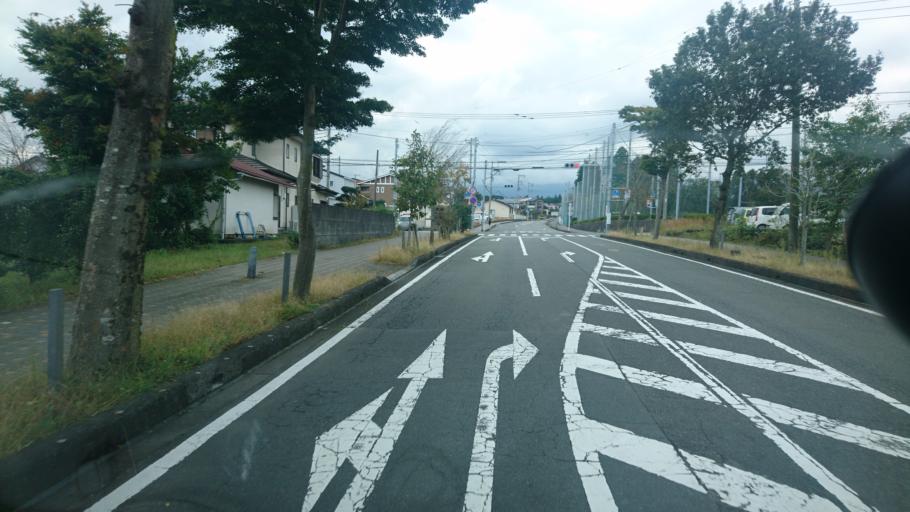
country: JP
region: Shizuoka
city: Gotemba
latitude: 35.3143
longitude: 138.9066
